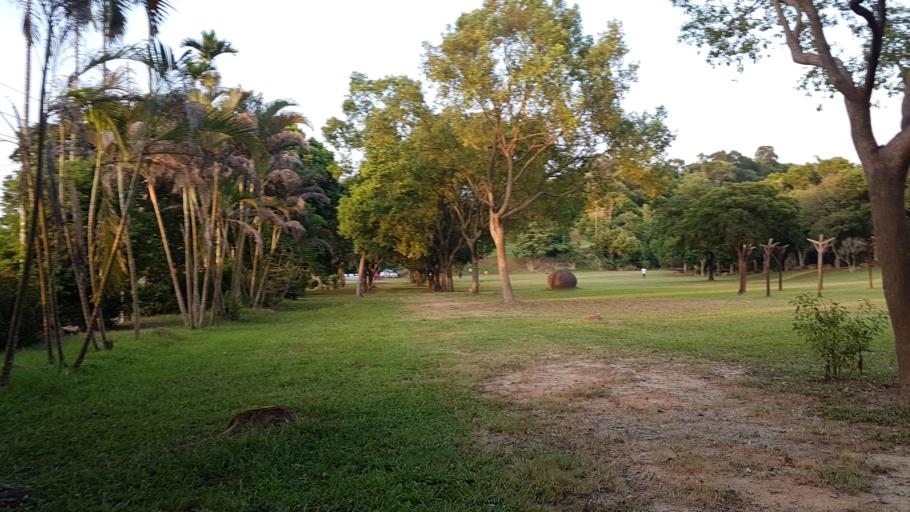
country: TW
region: Taiwan
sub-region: Chiayi
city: Jiayi Shi
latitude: 23.3578
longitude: 120.4672
